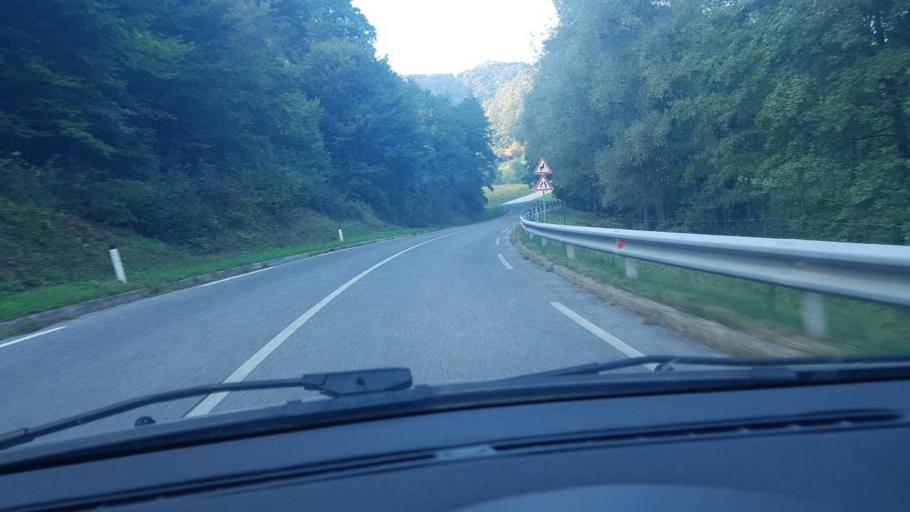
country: SI
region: Rogatec
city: Rogatec
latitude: 46.2592
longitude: 15.7021
